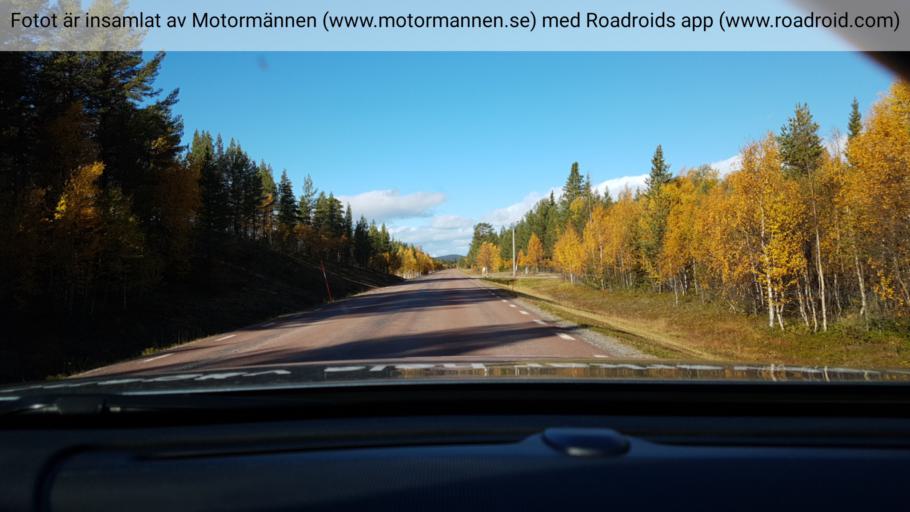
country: SE
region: Norrbotten
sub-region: Arjeplogs Kommun
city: Arjeplog
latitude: 66.0057
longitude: 18.1091
